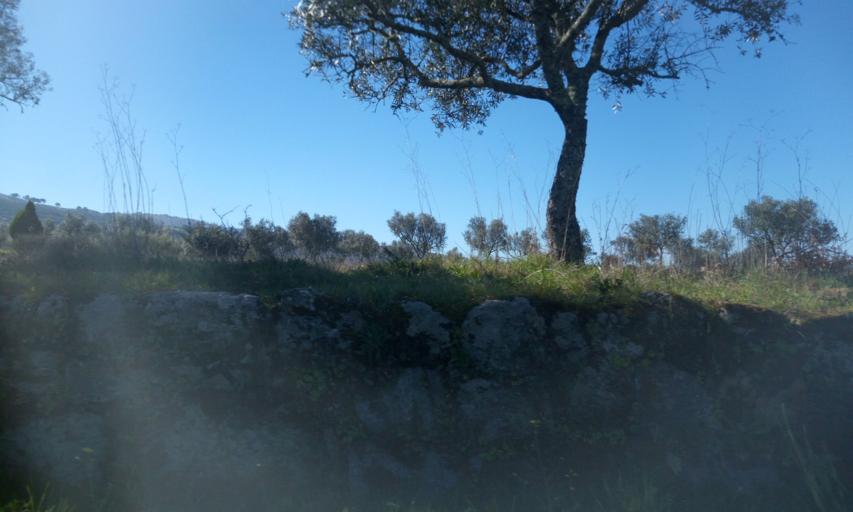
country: PT
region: Guarda
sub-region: Fornos de Algodres
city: Fornos de Algodres
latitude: 40.5250
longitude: -7.5549
